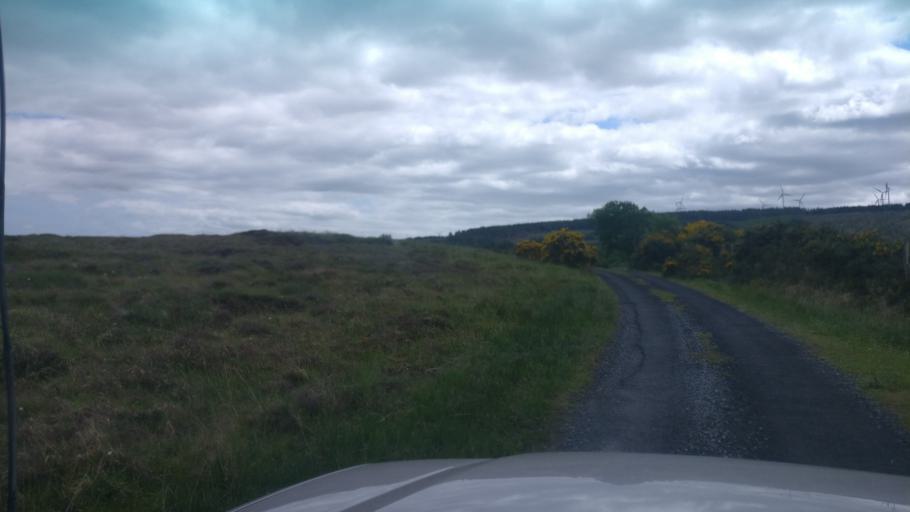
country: IE
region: Connaught
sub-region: County Galway
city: Loughrea
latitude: 53.1133
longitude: -8.6307
